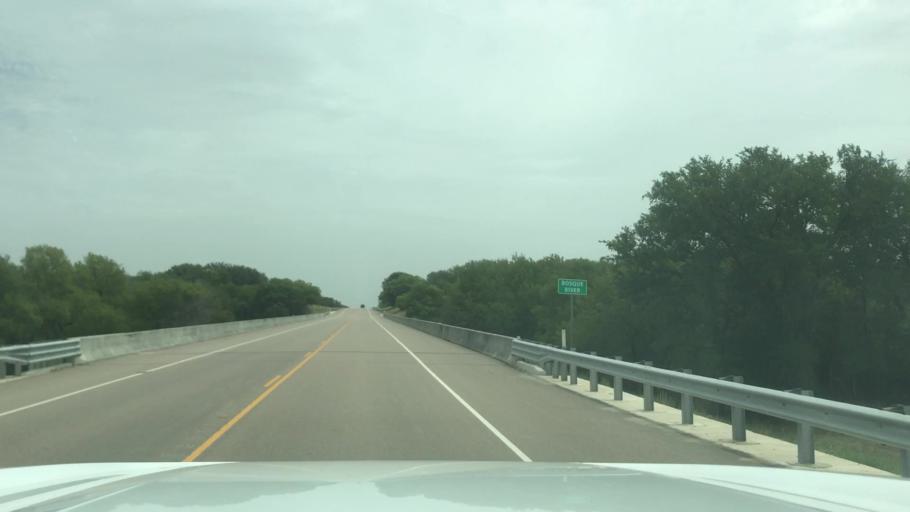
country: US
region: Texas
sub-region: Hamilton County
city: Hico
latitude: 31.9777
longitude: -97.8969
